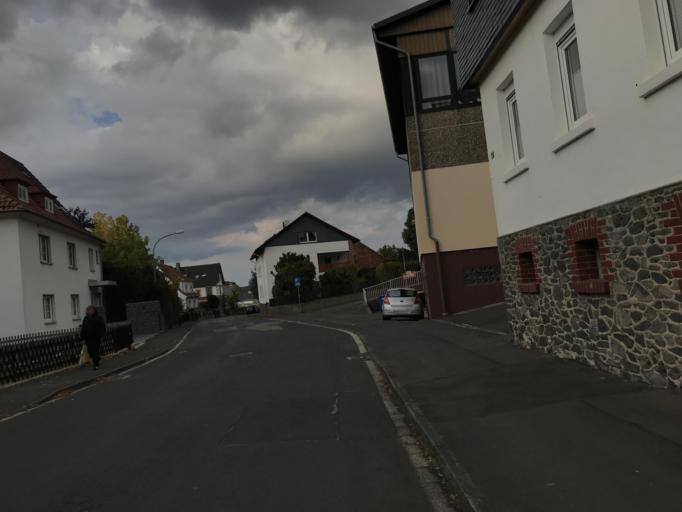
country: DE
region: Hesse
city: Borken
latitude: 51.0460
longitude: 9.2794
